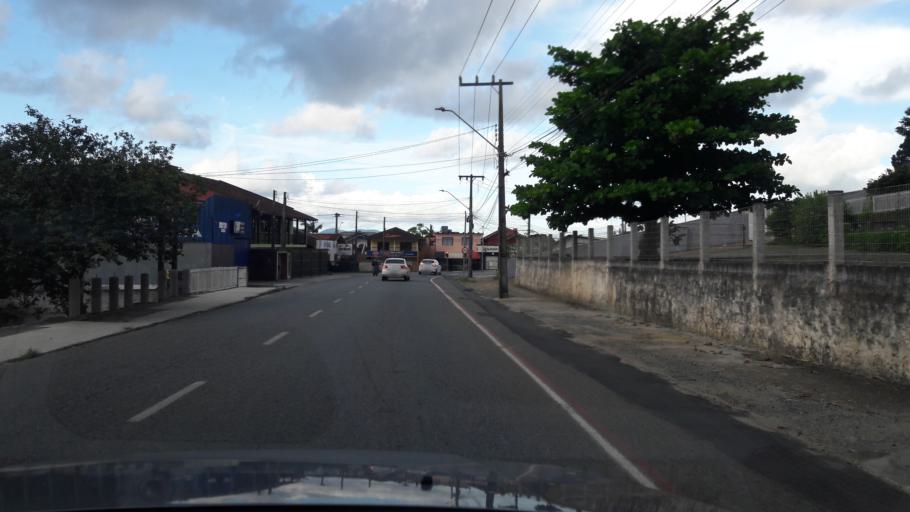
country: BR
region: Santa Catarina
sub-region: Joinville
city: Joinville
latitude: -26.3210
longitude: -48.8265
